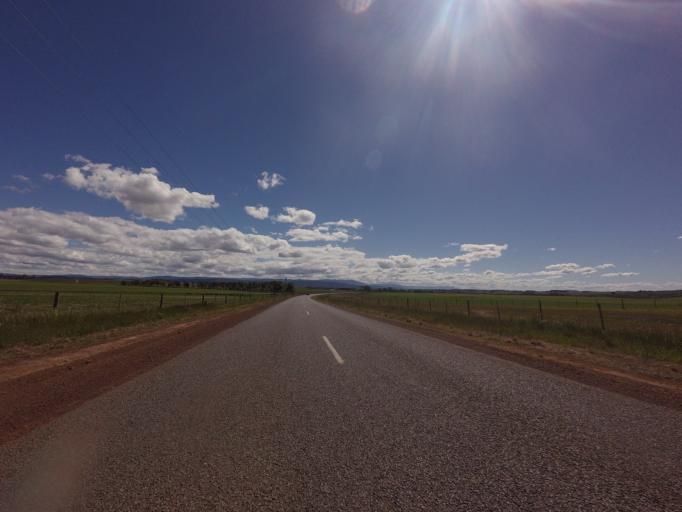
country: AU
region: Tasmania
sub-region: Northern Midlands
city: Evandale
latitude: -41.9401
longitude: 147.5565
